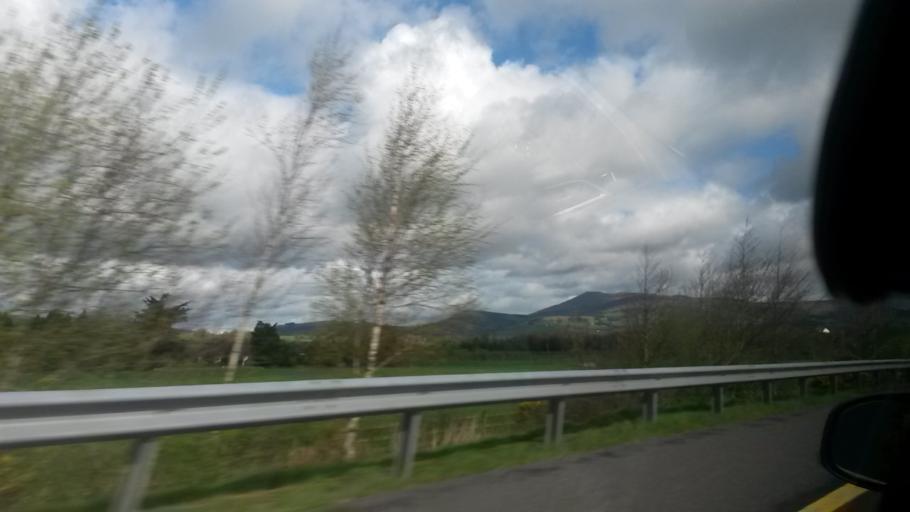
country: IE
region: Munster
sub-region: County Cork
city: Mitchelstown
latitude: 52.2654
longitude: -8.2469
